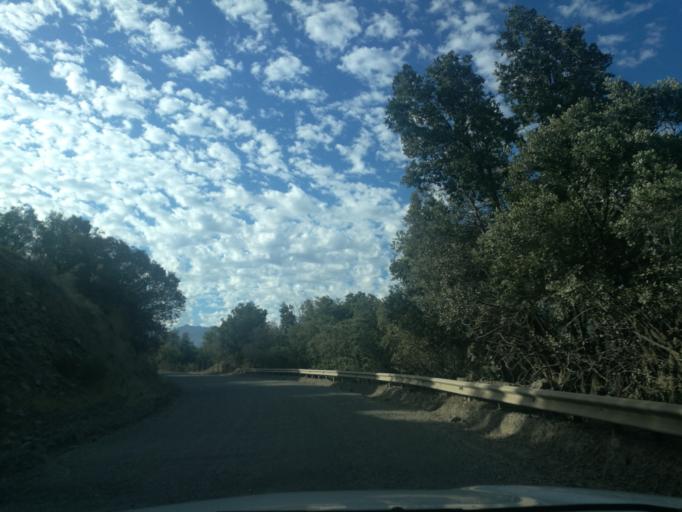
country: CL
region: O'Higgins
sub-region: Provincia de Cachapoal
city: Machali
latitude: -34.2569
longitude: -70.4633
